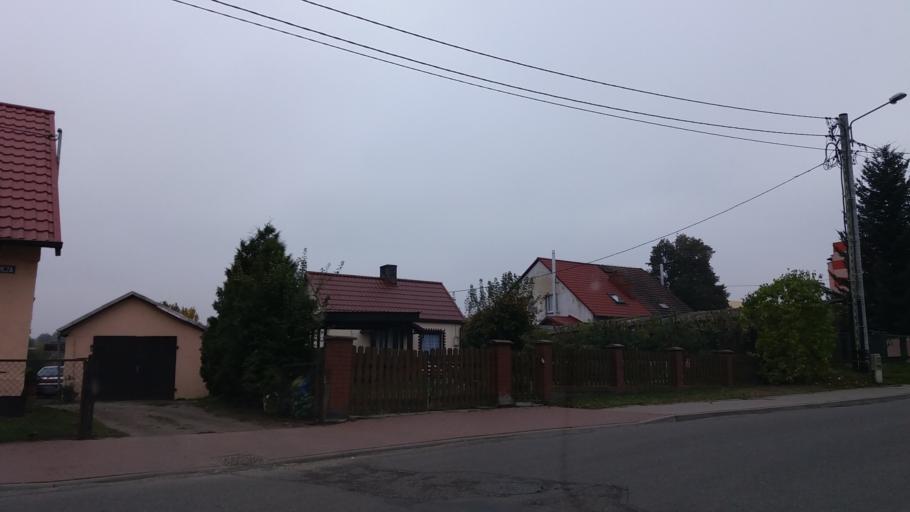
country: PL
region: West Pomeranian Voivodeship
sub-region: Powiat choszczenski
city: Bierzwnik
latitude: 53.0357
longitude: 15.6619
